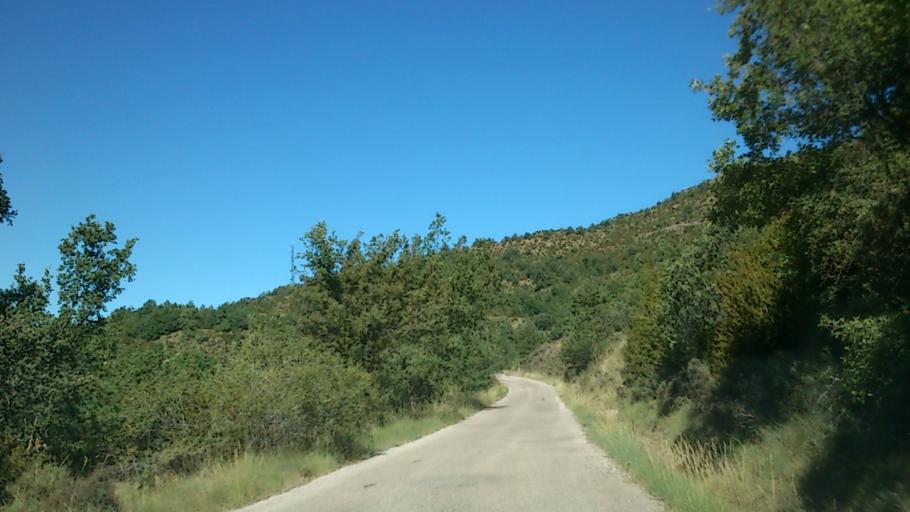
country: ES
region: Aragon
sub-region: Provincia de Huesca
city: Loporzano
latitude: 42.3171
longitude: -0.2688
